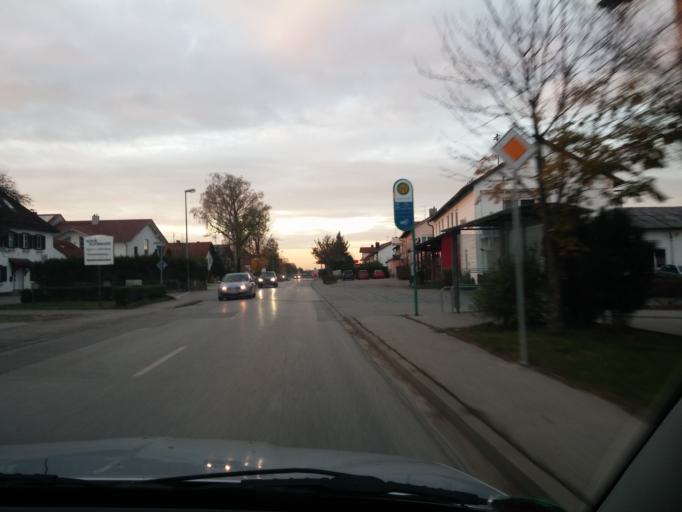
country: DE
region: Bavaria
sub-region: Upper Bavaria
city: Forstern
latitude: 48.1849
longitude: 11.9766
